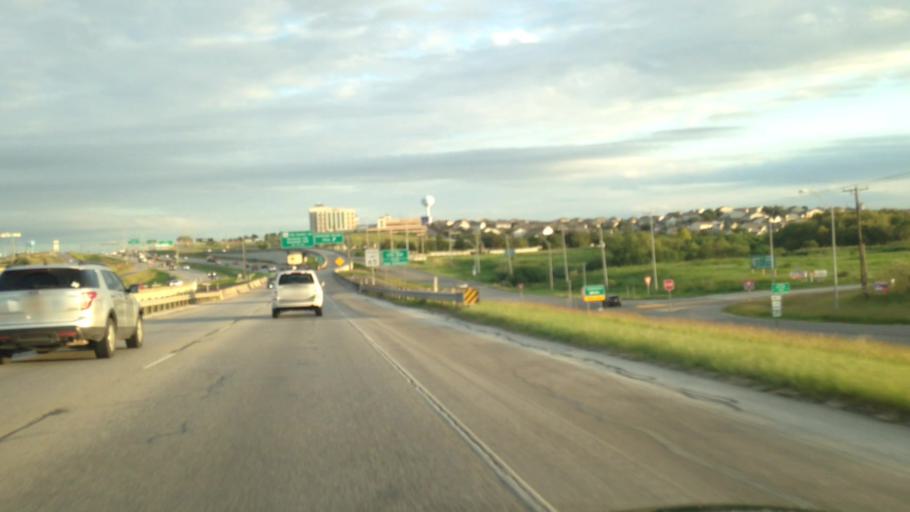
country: US
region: Texas
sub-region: Bexar County
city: Live Oak
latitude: 29.5794
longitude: -98.3435
